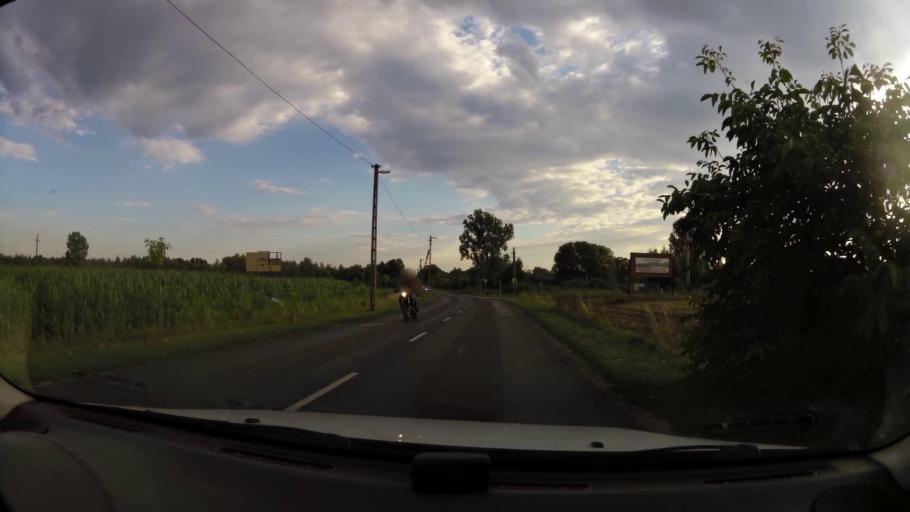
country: HU
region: Pest
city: Tapioszecso
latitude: 47.4473
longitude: 19.6018
